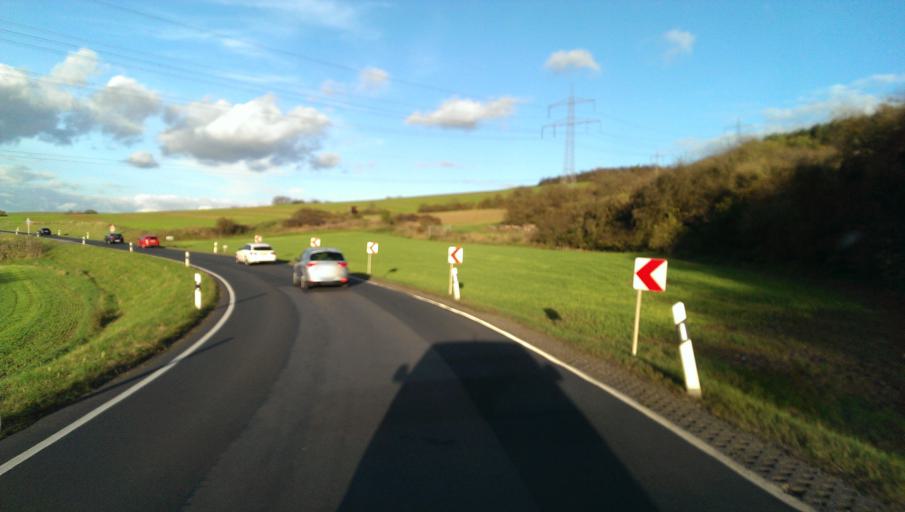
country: DE
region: Bavaria
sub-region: Regierungsbezirk Unterfranken
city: Arnstein
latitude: 49.9857
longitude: 9.9784
